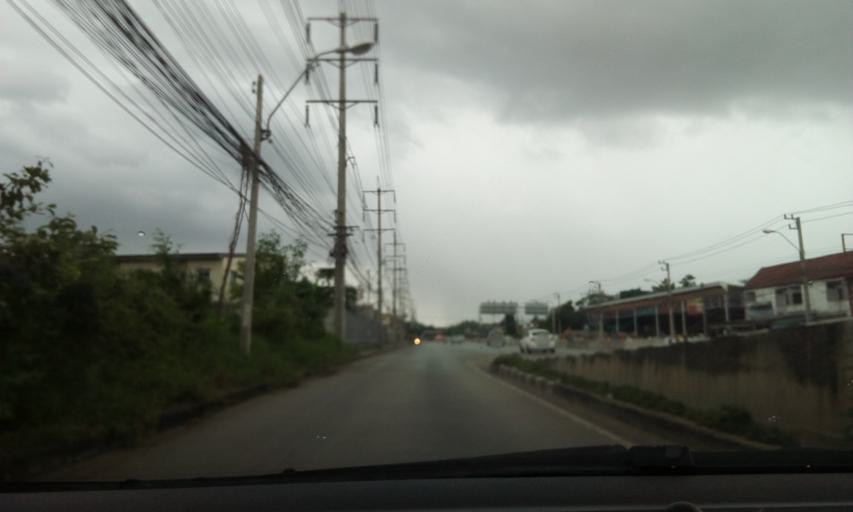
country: TH
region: Phra Nakhon Si Ayutthaya
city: Ban Bang Kadi Pathum Thani
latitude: 13.9642
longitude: 100.5508
